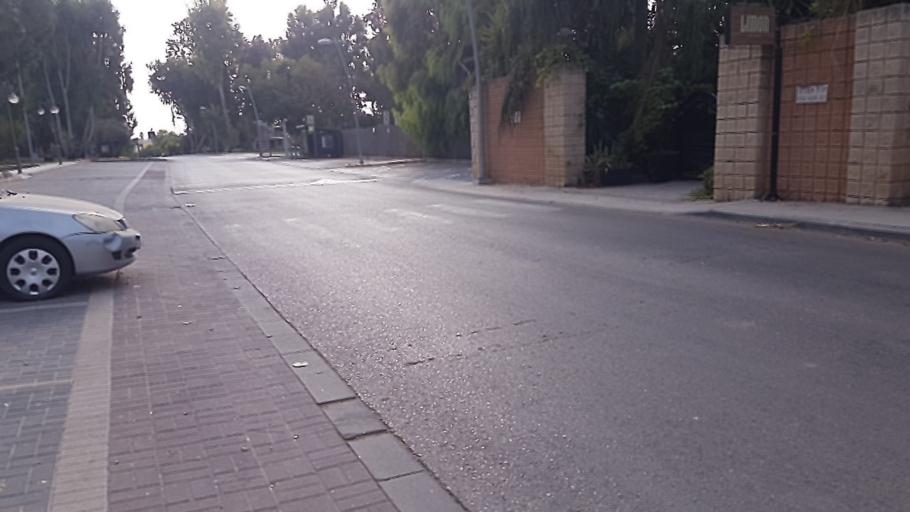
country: IL
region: Central District
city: Rosh Ha'Ayin
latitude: 32.0821
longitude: 34.9397
